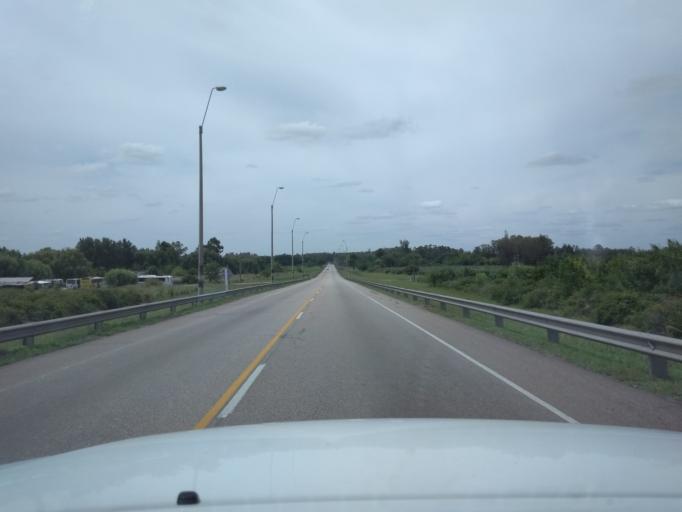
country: UY
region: Canelones
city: Canelones
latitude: -34.5414
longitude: -56.2740
